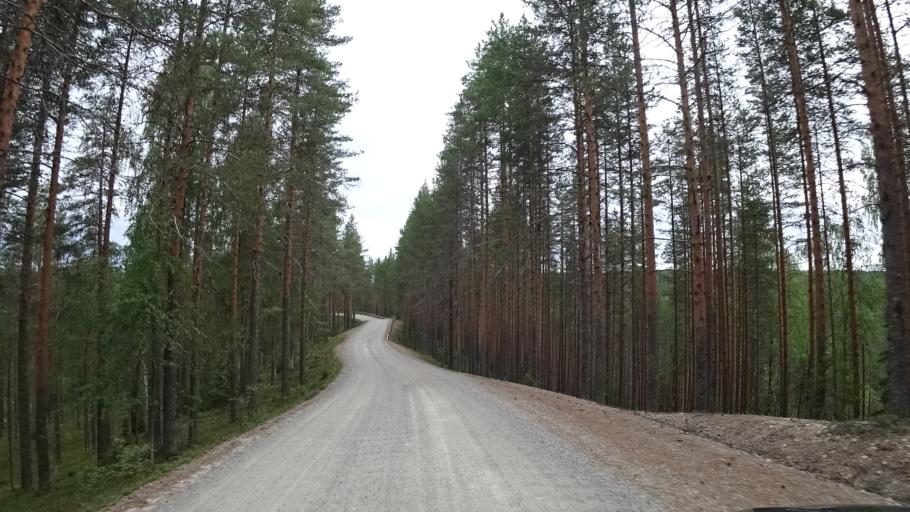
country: FI
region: North Karelia
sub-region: Pielisen Karjala
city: Lieksa
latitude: 63.2105
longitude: 30.4172
